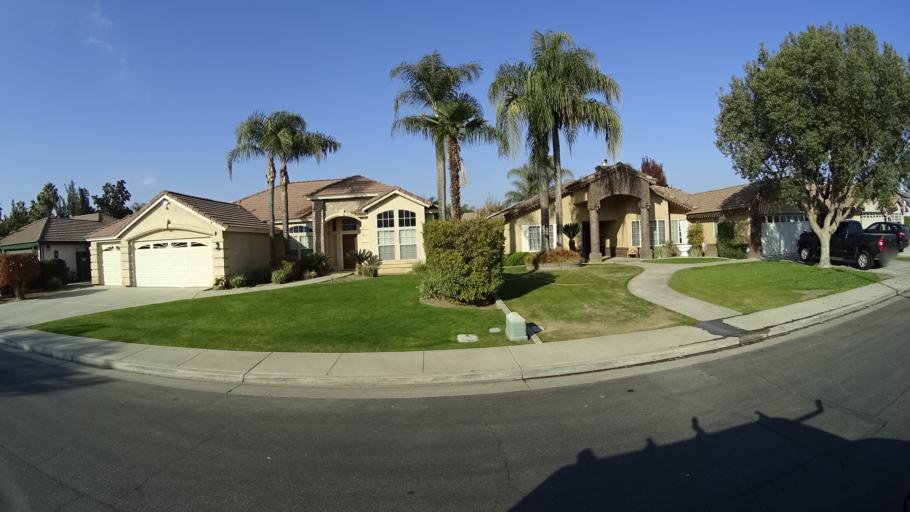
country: US
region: California
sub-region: Kern County
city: Rosedale
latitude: 35.3550
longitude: -119.1583
